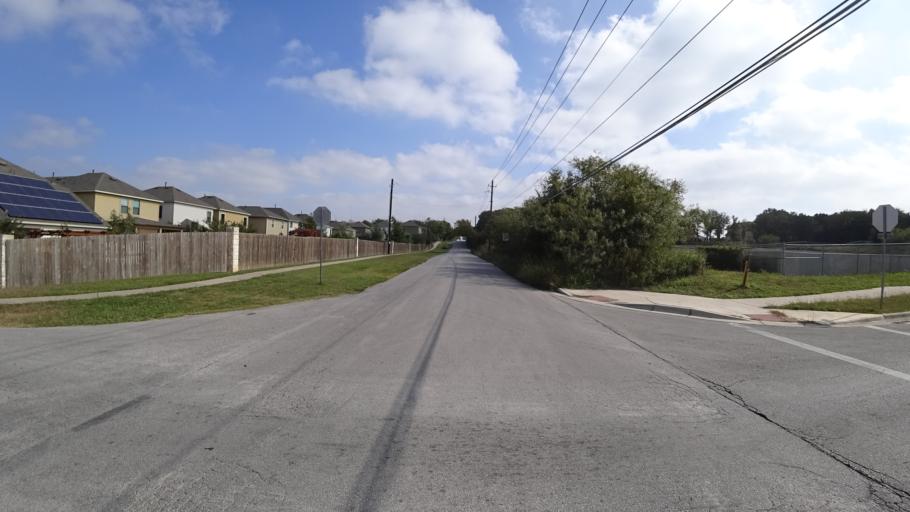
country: US
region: Texas
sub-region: Travis County
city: Shady Hollow
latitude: 30.1947
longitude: -97.8309
